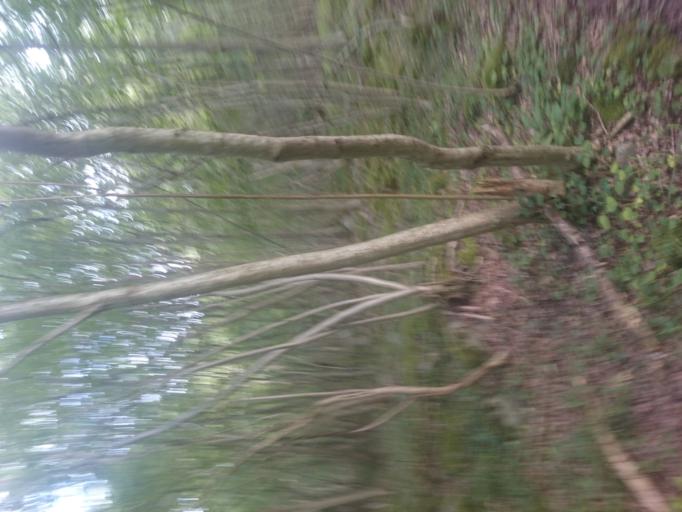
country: SE
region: Skane
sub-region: Simrishamns Kommun
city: Kivik
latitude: 55.6679
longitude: 14.2695
